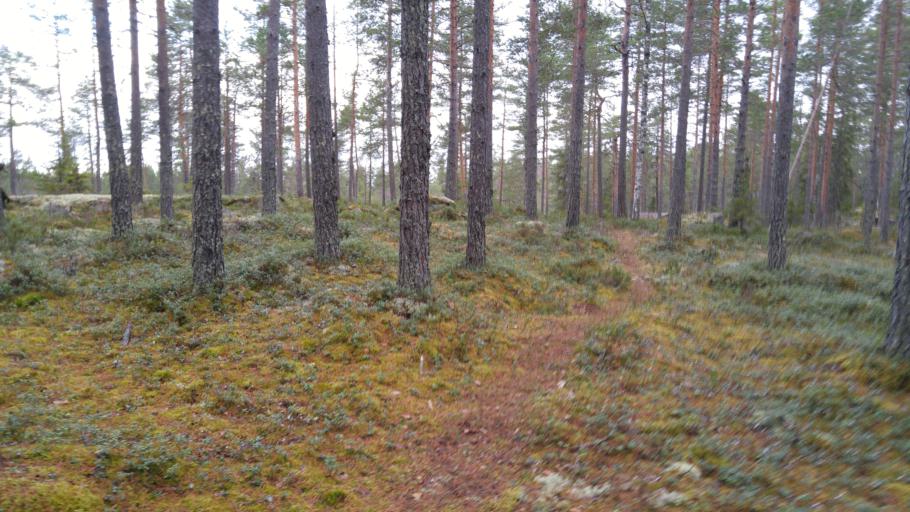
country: FI
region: Pirkanmaa
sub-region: Tampere
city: Kangasala
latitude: 61.6067
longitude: 23.9848
